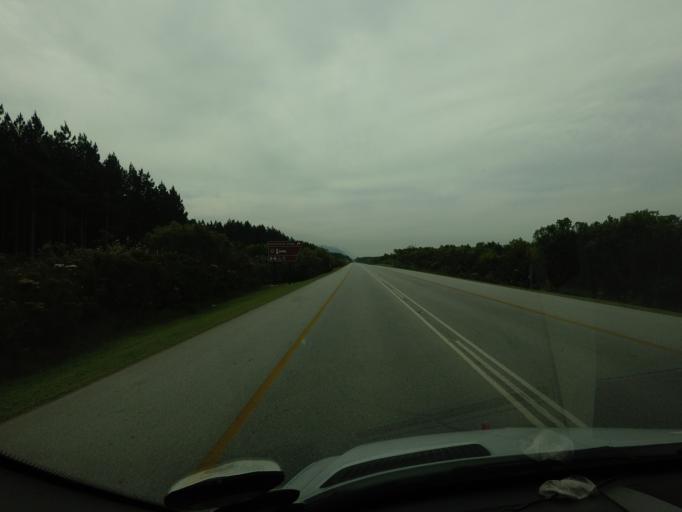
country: ZA
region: Eastern Cape
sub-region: Cacadu District Municipality
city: Kareedouw
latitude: -33.9660
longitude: 23.8802
